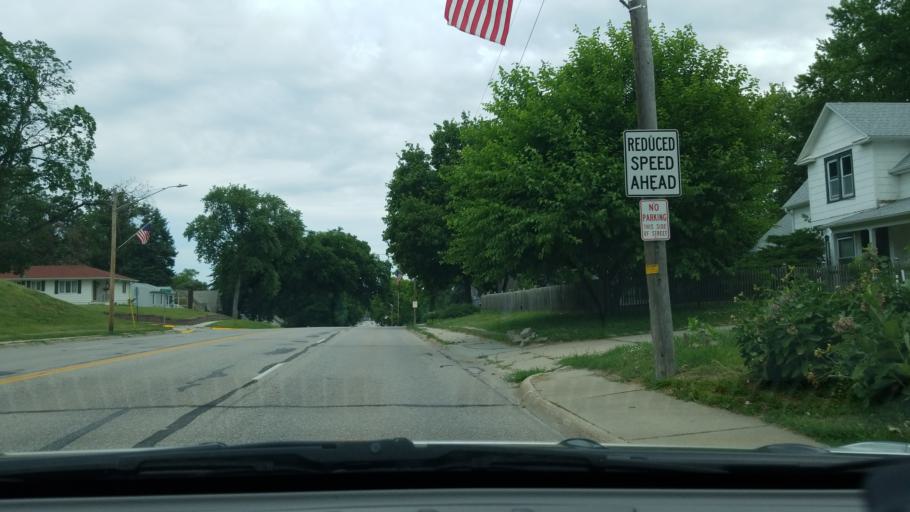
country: US
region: Nebraska
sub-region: Sarpy County
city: Papillion
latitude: 41.1480
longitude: -96.0429
